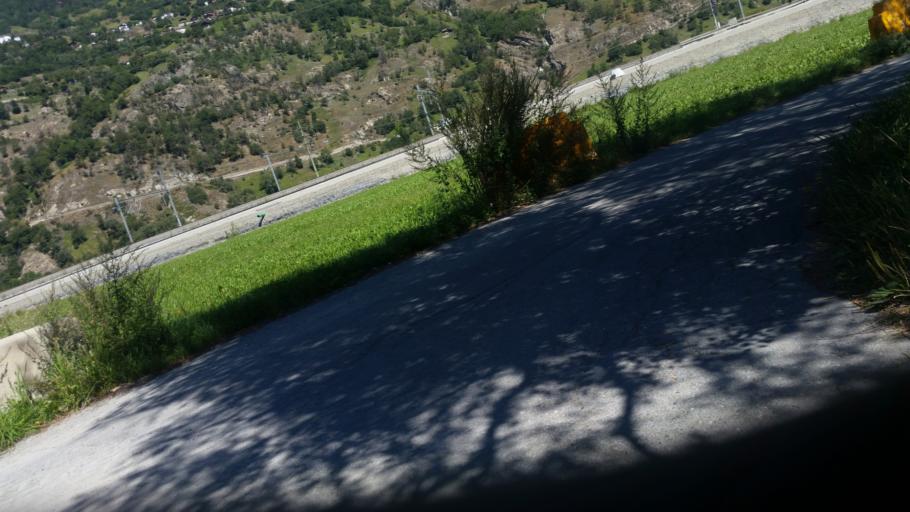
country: CH
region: Valais
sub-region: Visp District
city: Baltschieder
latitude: 46.3025
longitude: 7.8540
